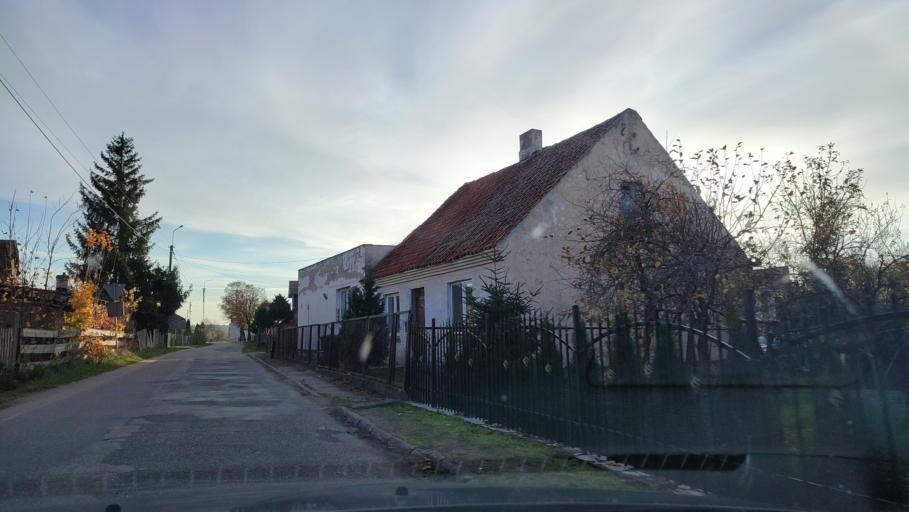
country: PL
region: Masovian Voivodeship
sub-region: Powiat mlawski
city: Dzierzgowo
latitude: 53.3131
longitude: 20.6730
